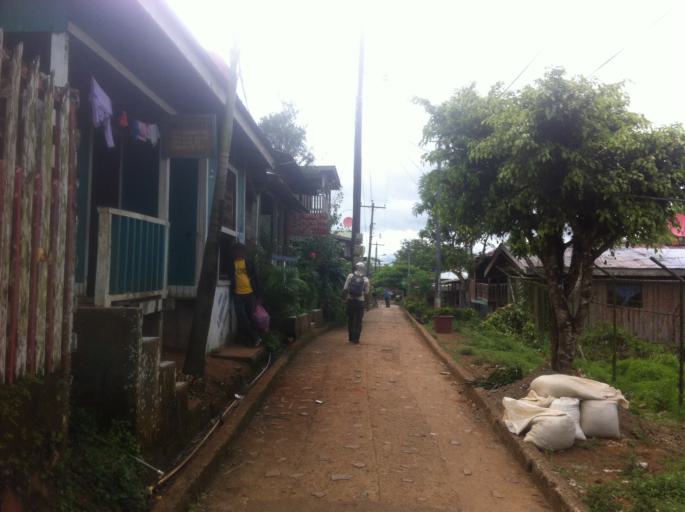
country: CR
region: Alajuela
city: Los Chiles
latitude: 11.0202
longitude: -84.3991
